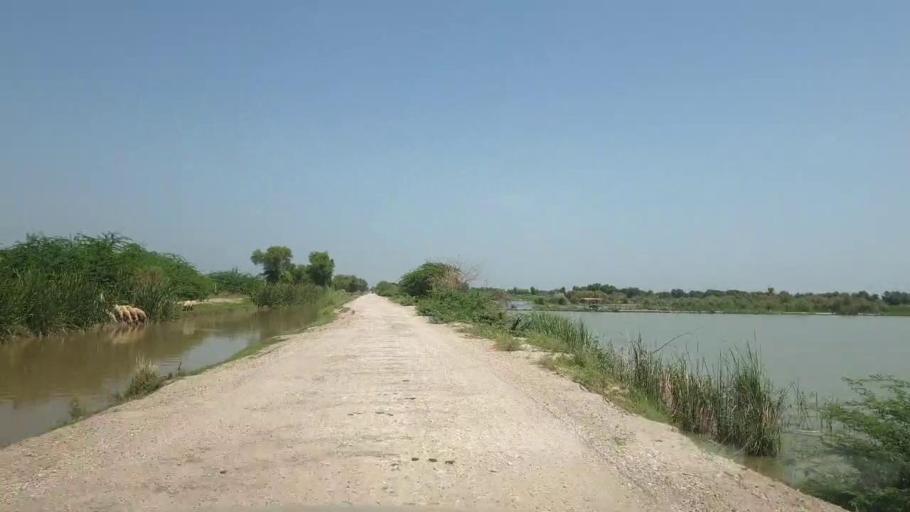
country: PK
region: Sindh
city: Rohri
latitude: 27.6392
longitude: 69.1023
